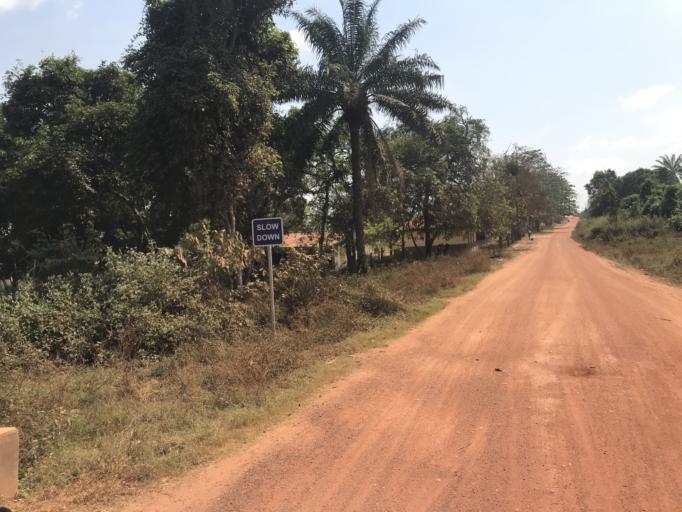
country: NG
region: Osun
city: Ifon
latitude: 7.8739
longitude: 4.4789
